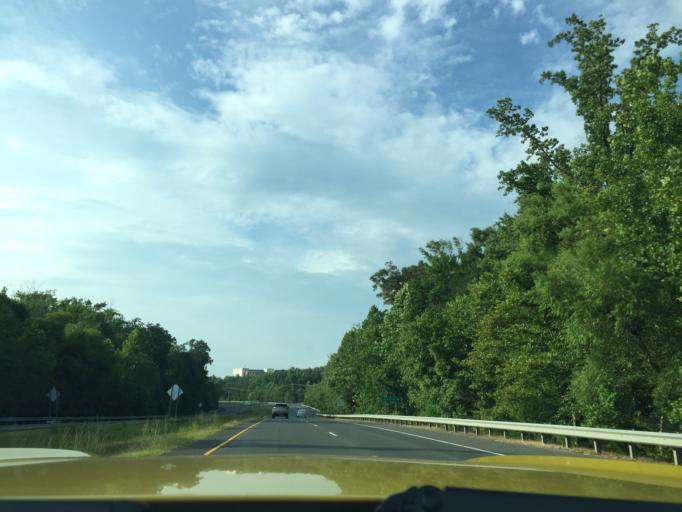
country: US
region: Virginia
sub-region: Fairfax County
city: Fort Belvoir
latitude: 38.7118
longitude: -77.1639
